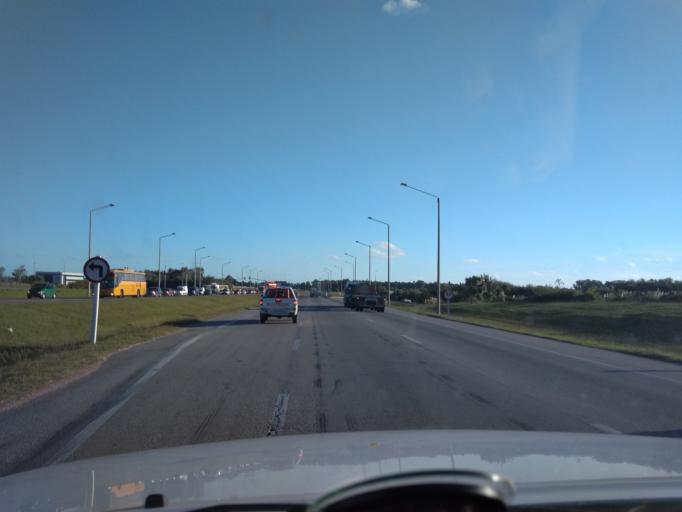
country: UY
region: Canelones
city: La Paz
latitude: -34.7723
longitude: -56.2696
